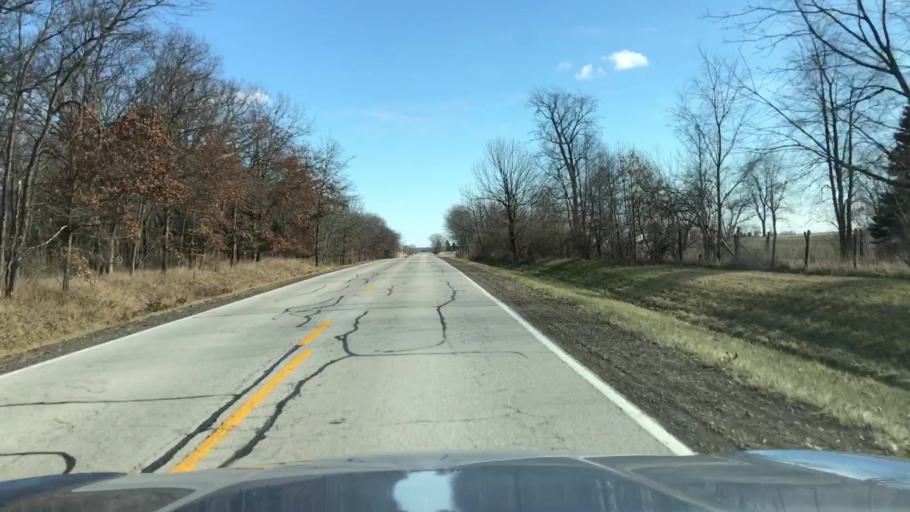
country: US
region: Illinois
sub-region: McLean County
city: Gridley
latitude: 40.6542
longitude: -88.8900
